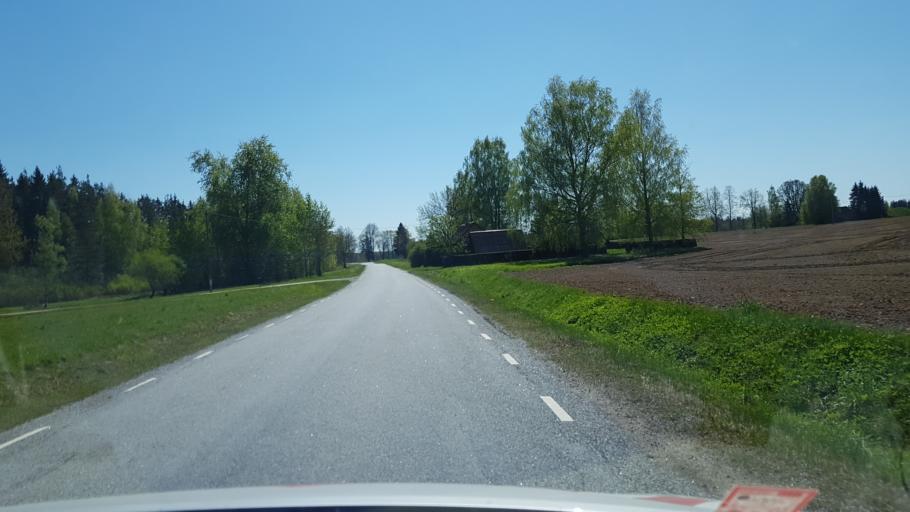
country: EE
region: Vorumaa
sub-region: Voru linn
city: Voru
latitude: 57.9149
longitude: 26.9559
